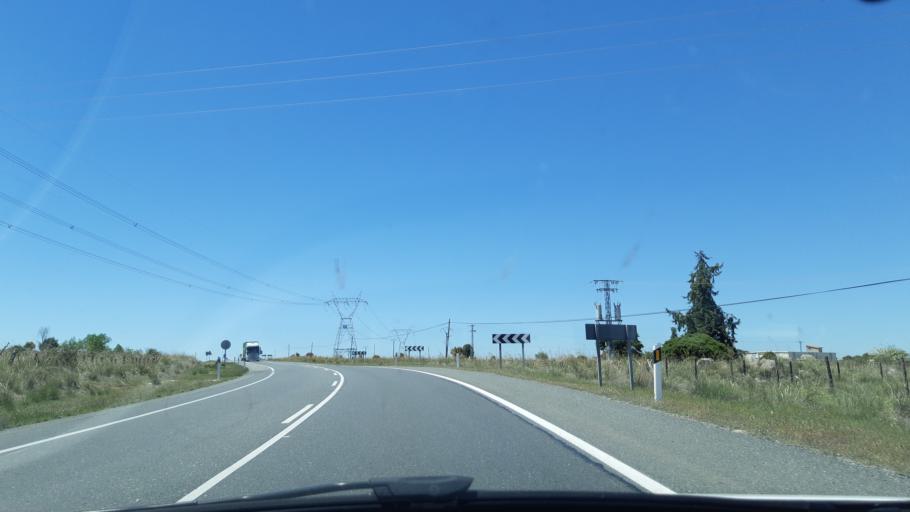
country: ES
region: Castille and Leon
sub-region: Provincia de Segovia
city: Villacastin
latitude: 40.7778
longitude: -4.3938
